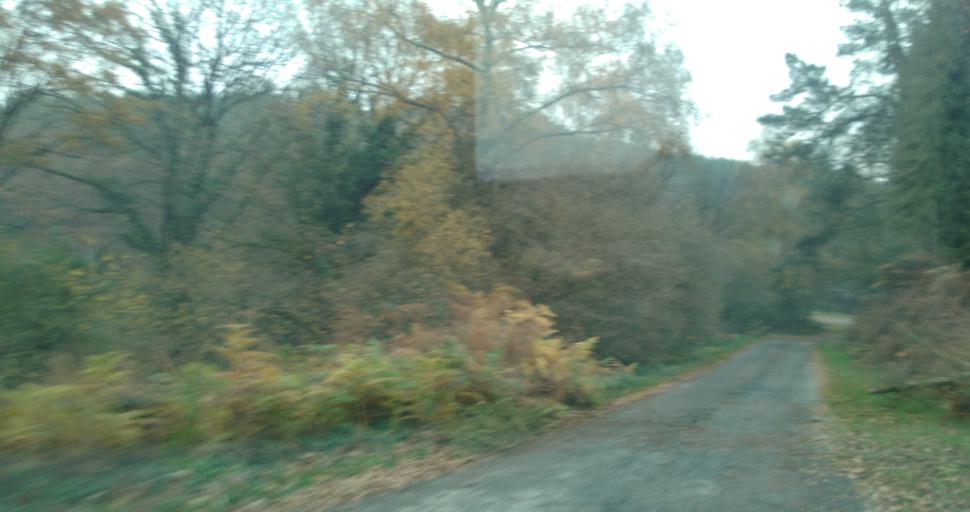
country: FR
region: Brittany
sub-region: Departement d'Ille-et-Vilaine
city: Iffendic
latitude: 48.0941
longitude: -2.0590
